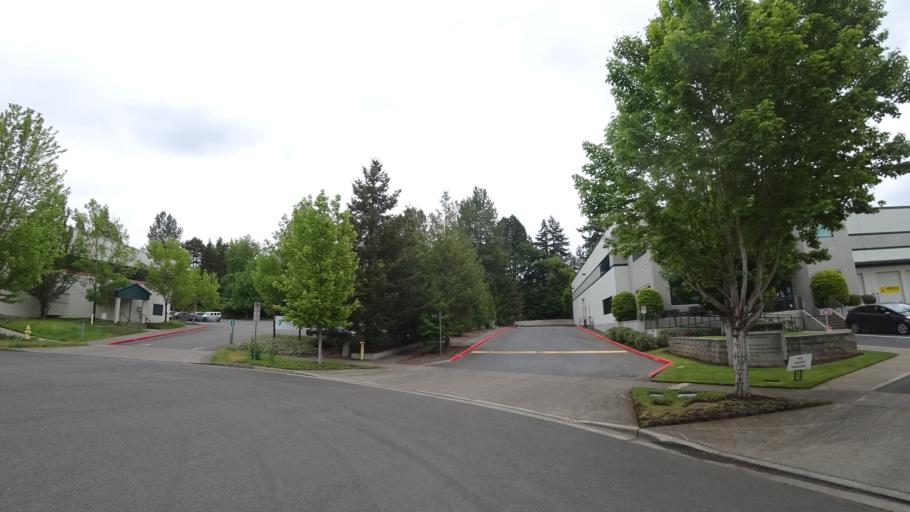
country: US
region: Oregon
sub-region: Washington County
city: Raleigh Hills
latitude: 45.4788
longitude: -122.7769
